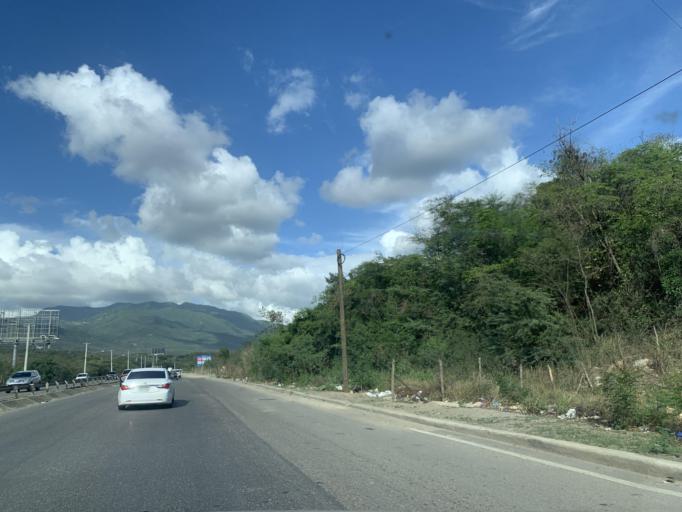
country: DO
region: Santiago
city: Villa Gonzalez
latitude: 19.5517
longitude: -70.8271
